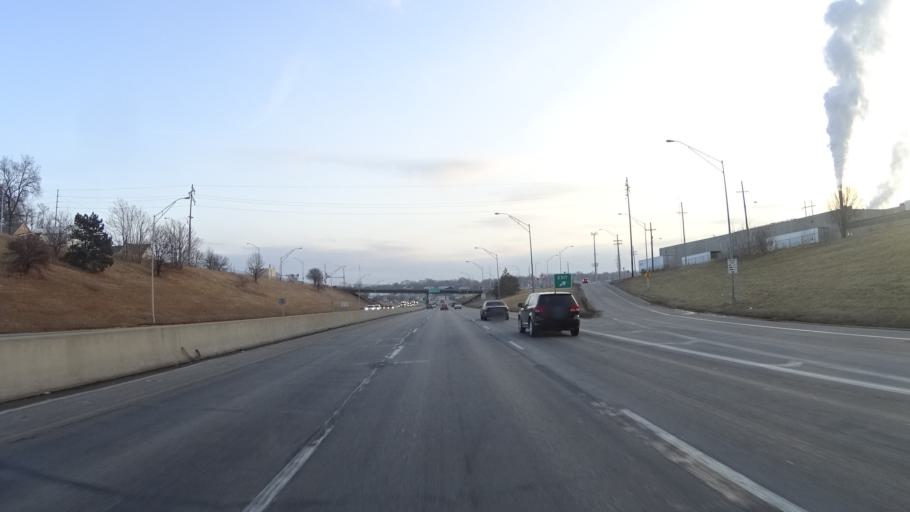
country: US
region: Nebraska
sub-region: Douglas County
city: Omaha
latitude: 41.2082
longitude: -95.9494
